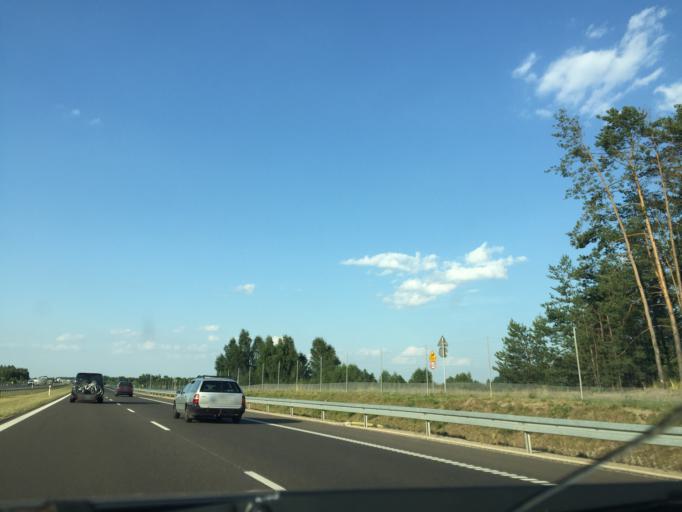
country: PL
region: Masovian Voivodeship
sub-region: Powiat radomski
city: Jedlinsk
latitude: 51.4890
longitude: 21.0701
